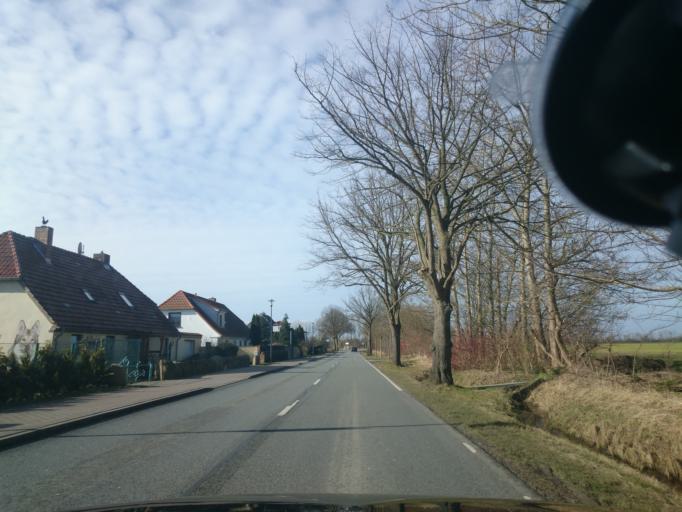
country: DE
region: Mecklenburg-Vorpommern
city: Elmenhorst
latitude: 54.1598
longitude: 11.9886
